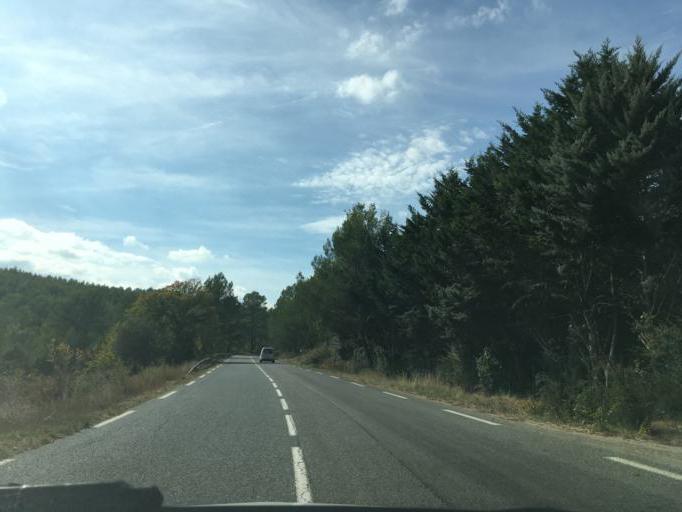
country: FR
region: Provence-Alpes-Cote d'Azur
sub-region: Departement du Var
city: Flayosc
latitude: 43.5430
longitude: 6.3555
